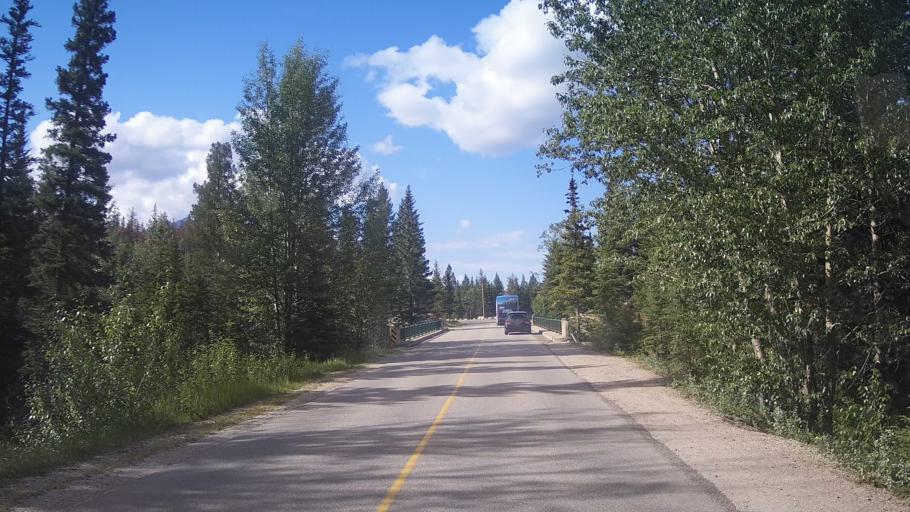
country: CA
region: Alberta
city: Jasper Park Lodge
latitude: 52.8649
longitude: -118.0705
